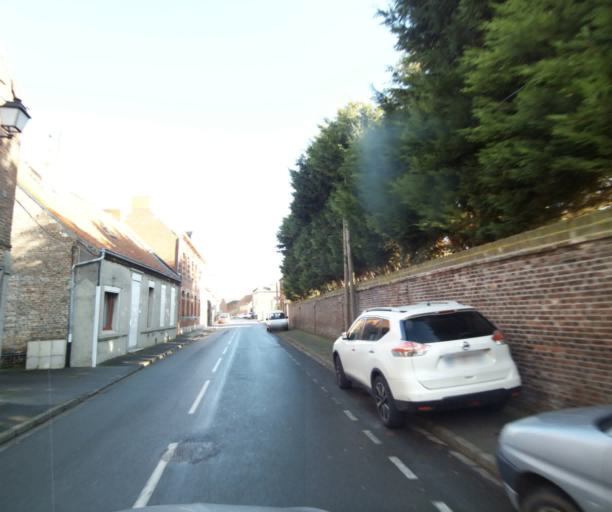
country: FR
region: Nord-Pas-de-Calais
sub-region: Departement du Nord
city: Preseau
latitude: 50.3100
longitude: 3.5742
